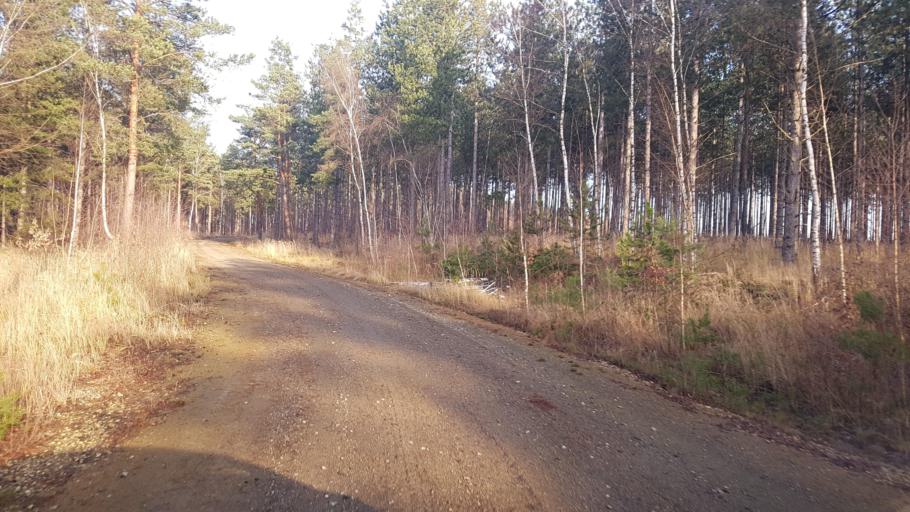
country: DE
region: Brandenburg
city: Lauchhammer
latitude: 51.5226
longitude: 13.6862
